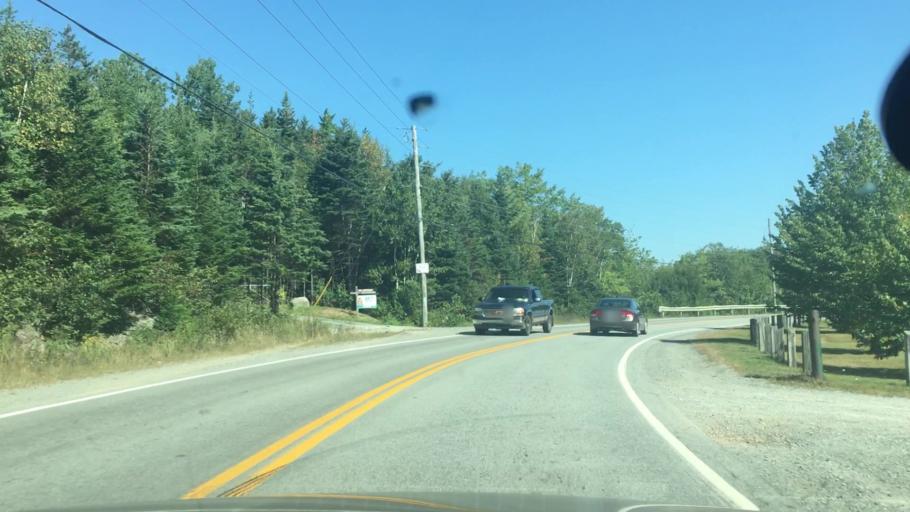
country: CA
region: Nova Scotia
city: New Glasgow
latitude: 44.9271
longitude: -62.5461
